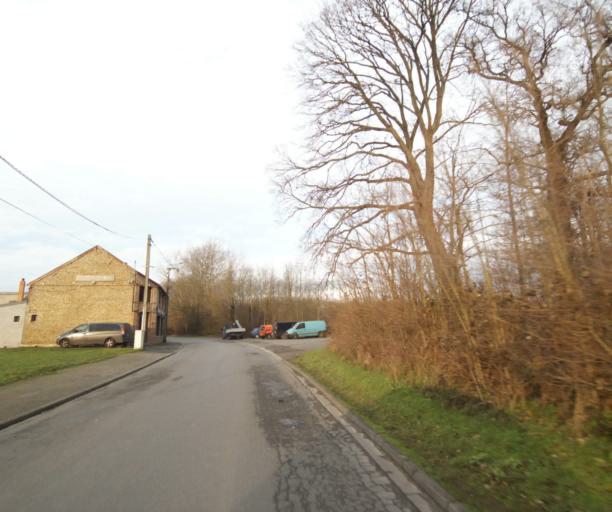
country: FR
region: Nord-Pas-de-Calais
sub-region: Departement du Nord
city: Conde-sur-l'Escaut
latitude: 50.4700
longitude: 3.6044
